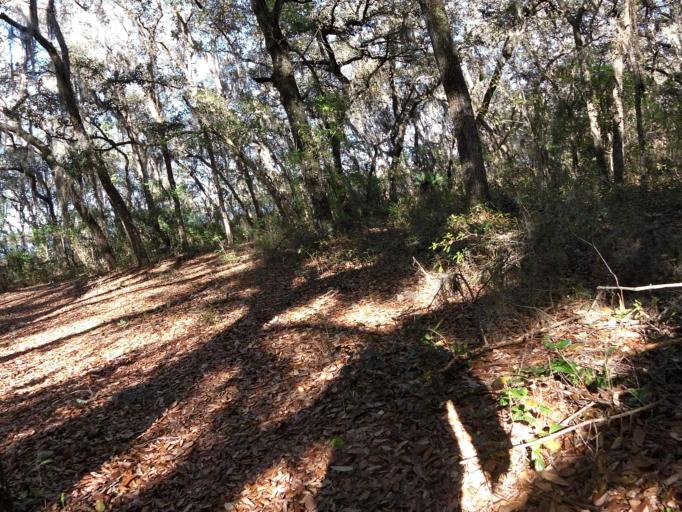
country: US
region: Florida
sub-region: Clay County
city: Keystone Heights
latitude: 29.8197
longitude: -82.0211
